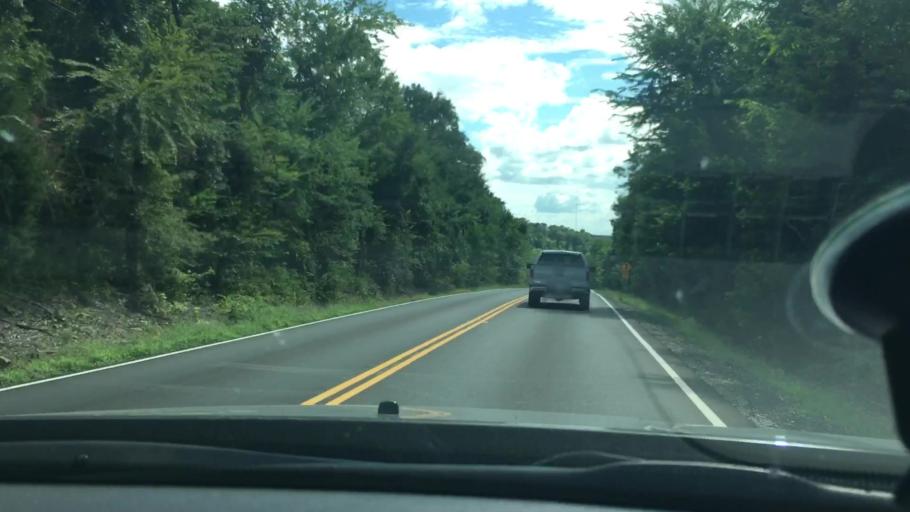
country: US
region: Oklahoma
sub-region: Sequoyah County
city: Vian
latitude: 35.6543
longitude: -94.9524
